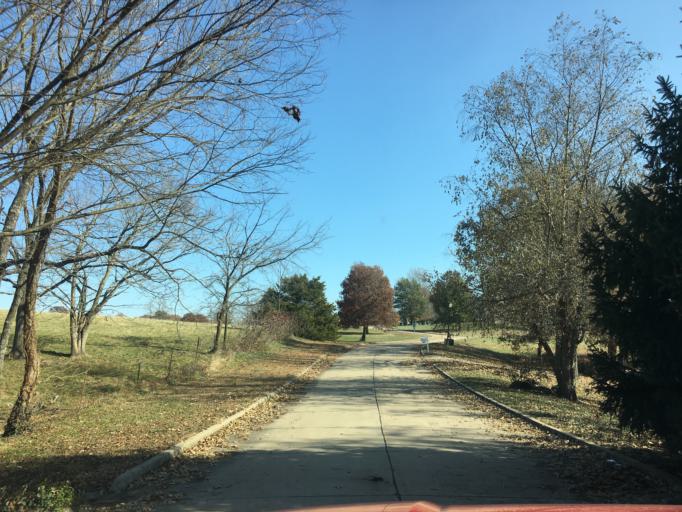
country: US
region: Missouri
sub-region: Cole County
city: Wardsville
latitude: 38.4840
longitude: -92.1806
